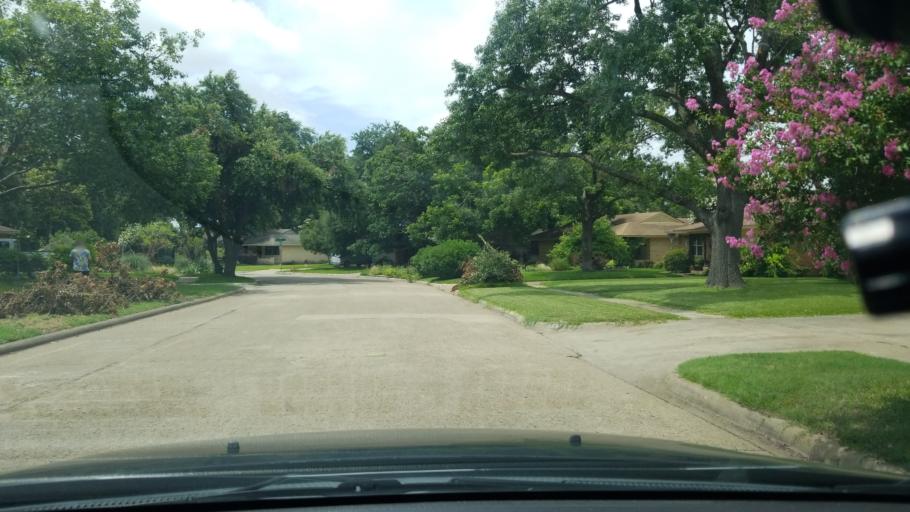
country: US
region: Texas
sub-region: Dallas County
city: Highland Park
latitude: 32.8282
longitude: -96.6926
